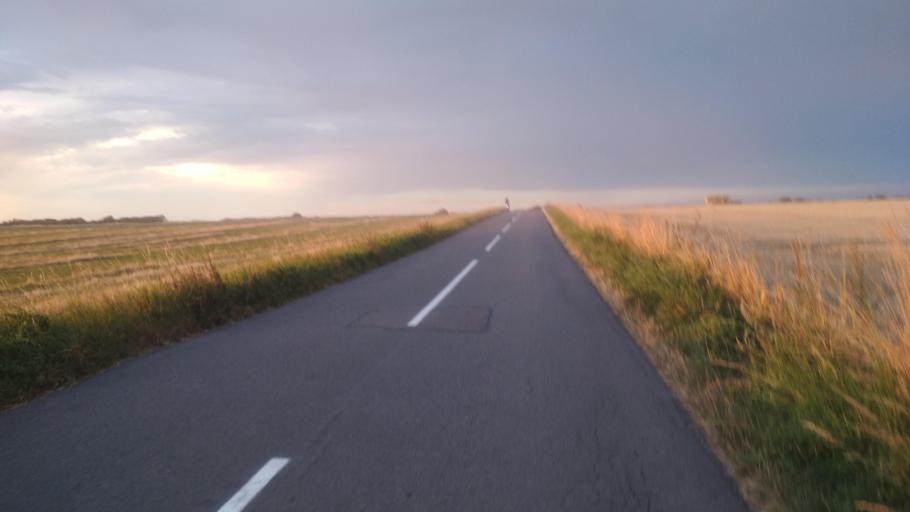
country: DK
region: Capital Region
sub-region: Bornholm Kommune
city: Akirkeby
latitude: 55.0283
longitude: 14.9109
